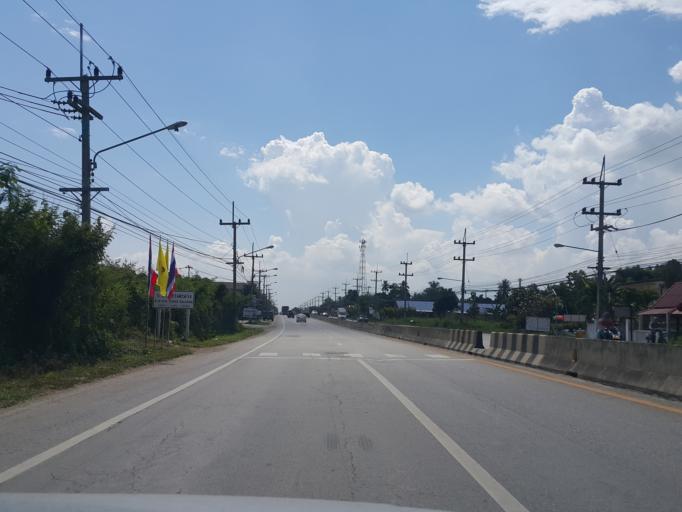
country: TH
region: Chiang Mai
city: Mae Taeng
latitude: 19.0195
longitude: 98.9445
